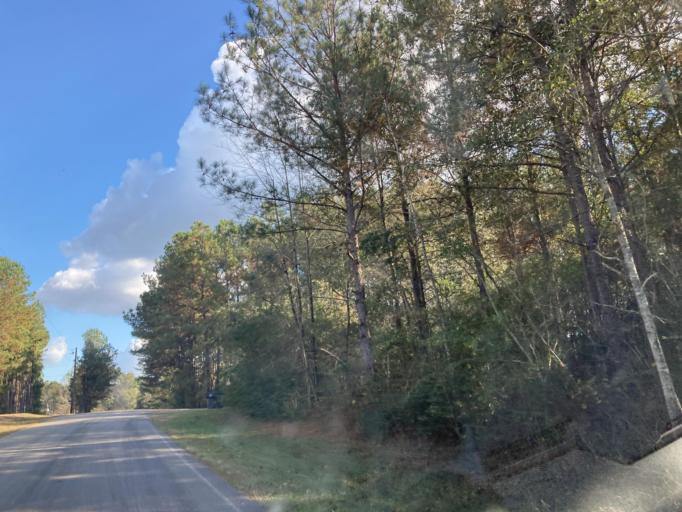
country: US
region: Mississippi
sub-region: Lamar County
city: Sumrall
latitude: 31.4275
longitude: -89.6457
